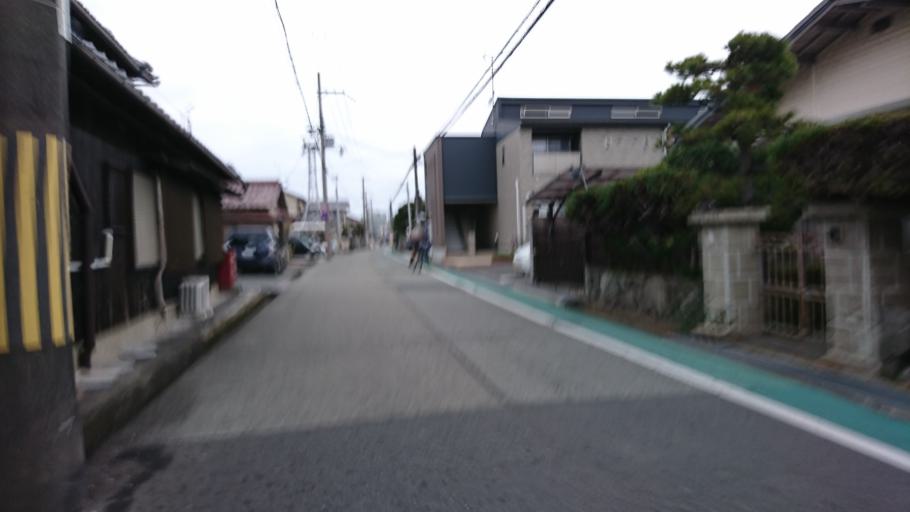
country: JP
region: Hyogo
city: Kakogawacho-honmachi
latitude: 34.7411
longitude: 134.8718
